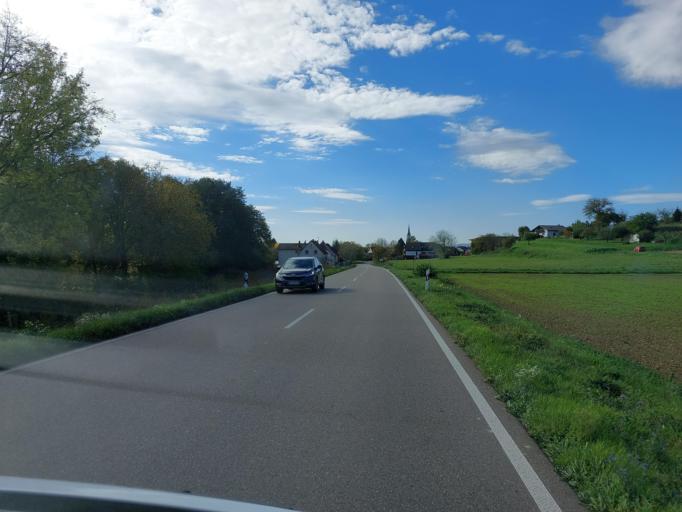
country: DE
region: Baden-Wuerttemberg
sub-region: Freiburg Region
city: Teningen
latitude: 48.1442
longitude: 7.8126
